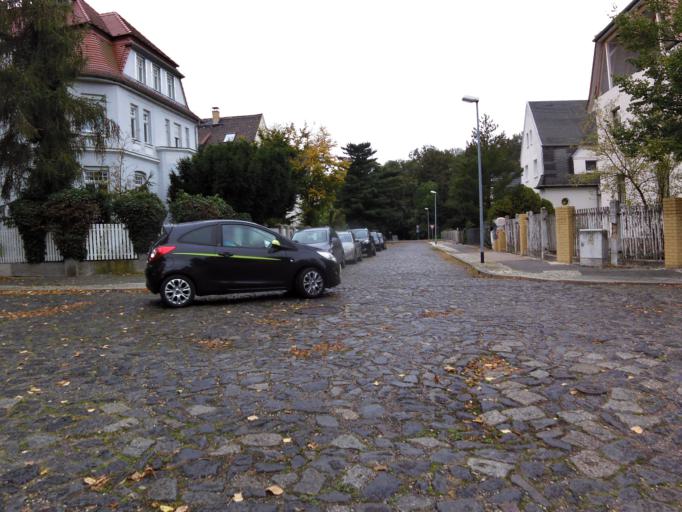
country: DE
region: Saxony
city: Markkleeberg
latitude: 51.2900
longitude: 12.3709
